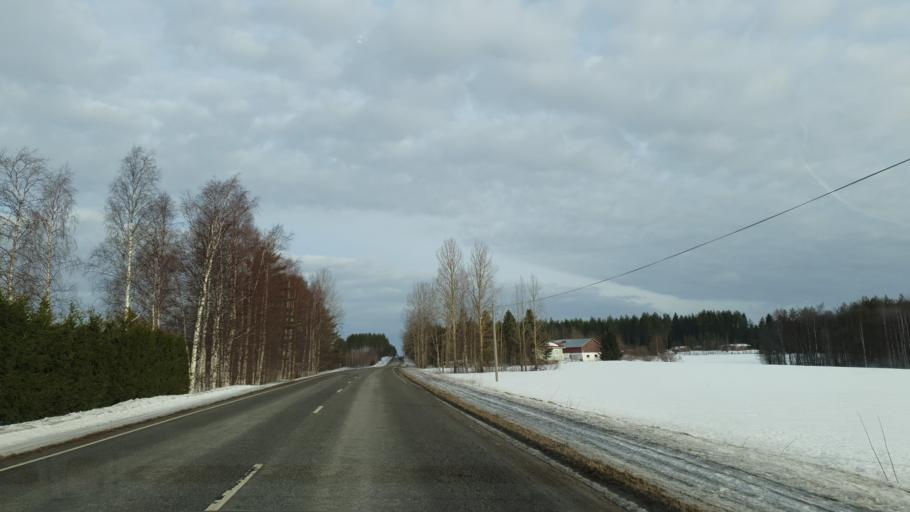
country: FI
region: Kainuu
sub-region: Kajaani
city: Vuokatti
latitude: 64.1762
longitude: 28.1977
